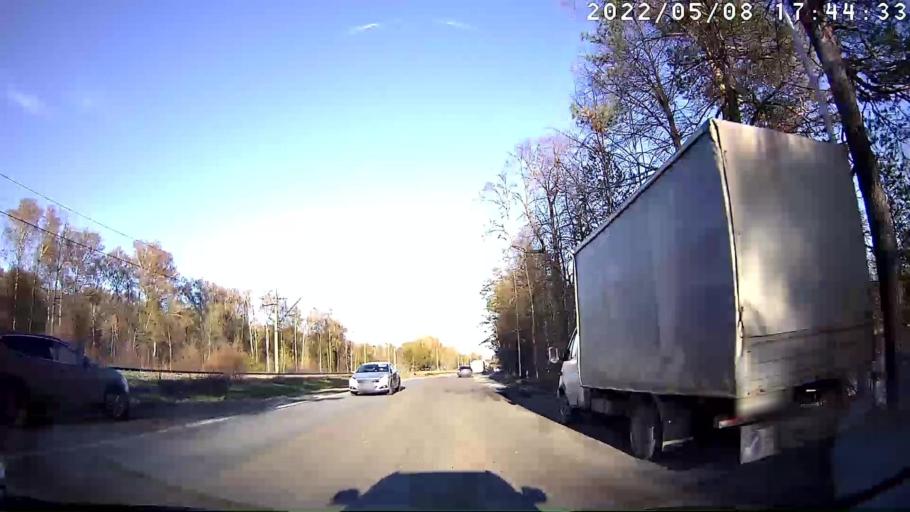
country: RU
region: Mariy-El
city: Volzhsk
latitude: 55.8440
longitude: 48.4158
